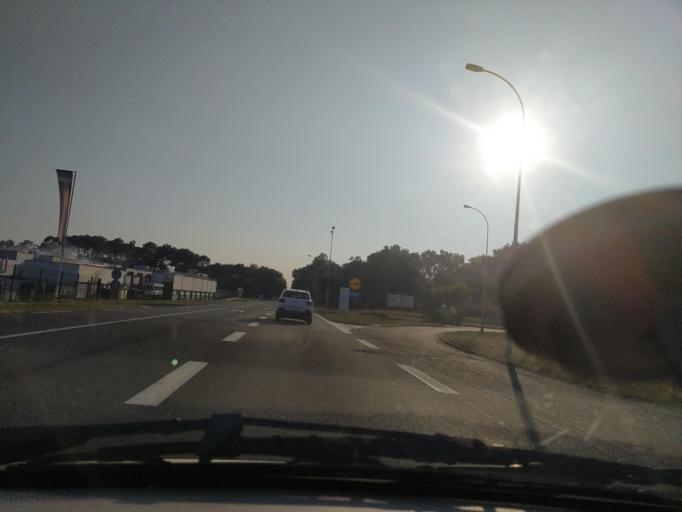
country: FR
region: Aquitaine
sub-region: Departement des Landes
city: Saint-Geours-de-Maremne
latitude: 43.6833
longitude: -1.2412
